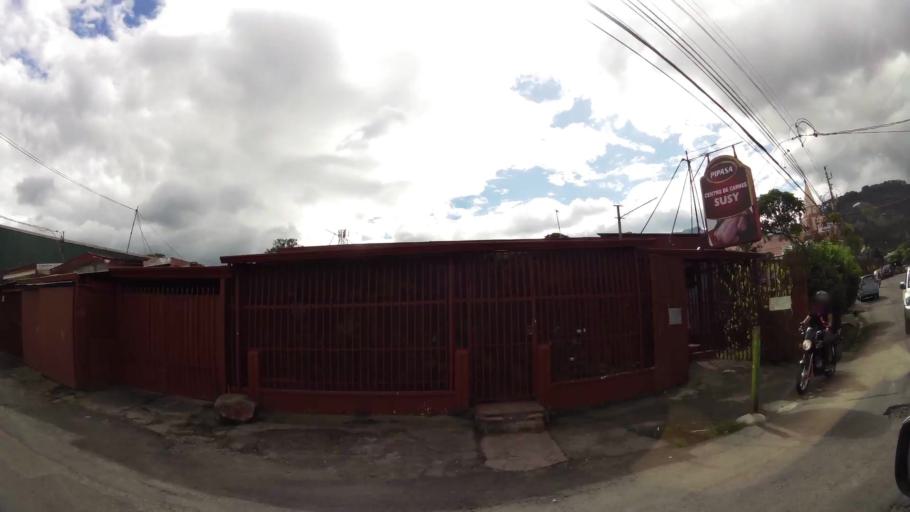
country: CR
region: San Jose
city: San Juan de Dios
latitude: 9.8794
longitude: -84.0820
